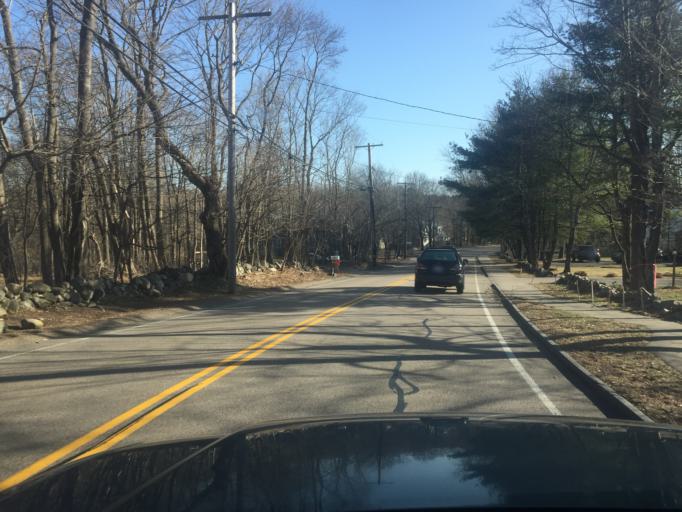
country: US
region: Massachusetts
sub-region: Norfolk County
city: Millis-Clicquot
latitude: 42.1435
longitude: -71.3562
